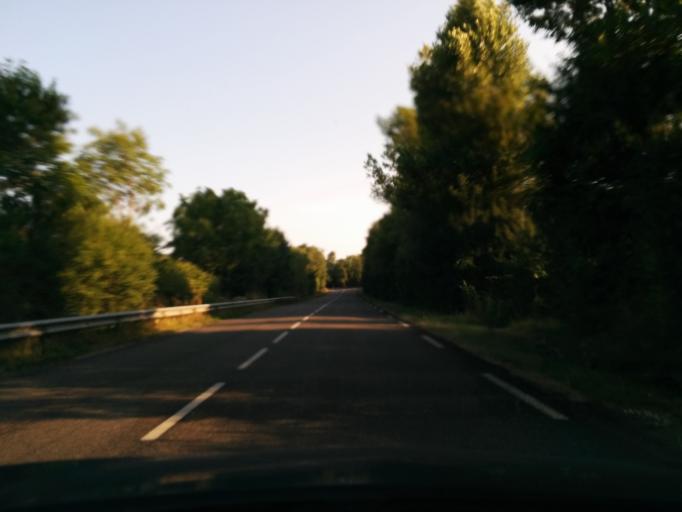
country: FR
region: Midi-Pyrenees
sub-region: Departement du Lot
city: Le Vigan
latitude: 44.6567
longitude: 1.4773
